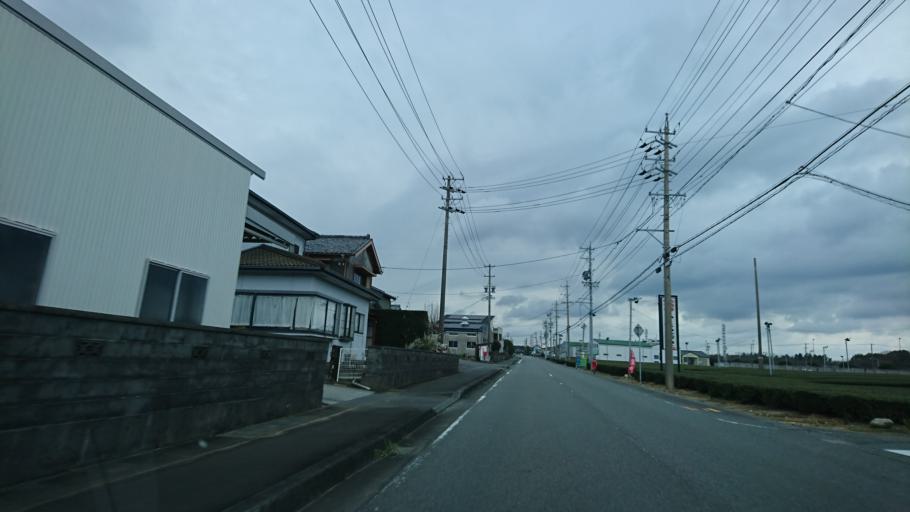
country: JP
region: Shizuoka
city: Shimada
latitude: 34.7575
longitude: 138.1590
